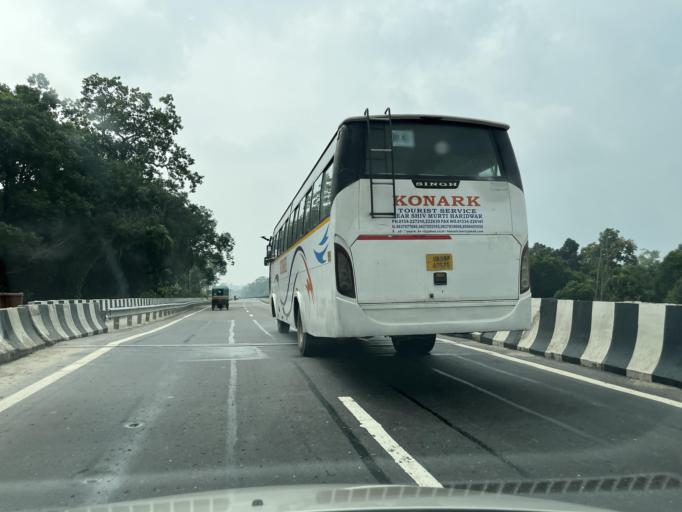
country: IN
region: Uttarakhand
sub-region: Dehradun
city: Raiwala
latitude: 30.0673
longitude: 78.2082
